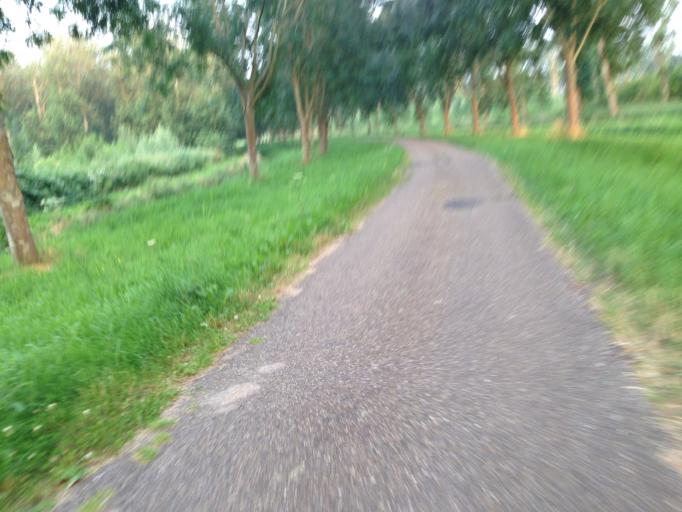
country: NL
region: Flevoland
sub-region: Gemeente Almere
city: Almere Stad
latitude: 52.4032
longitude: 5.2313
